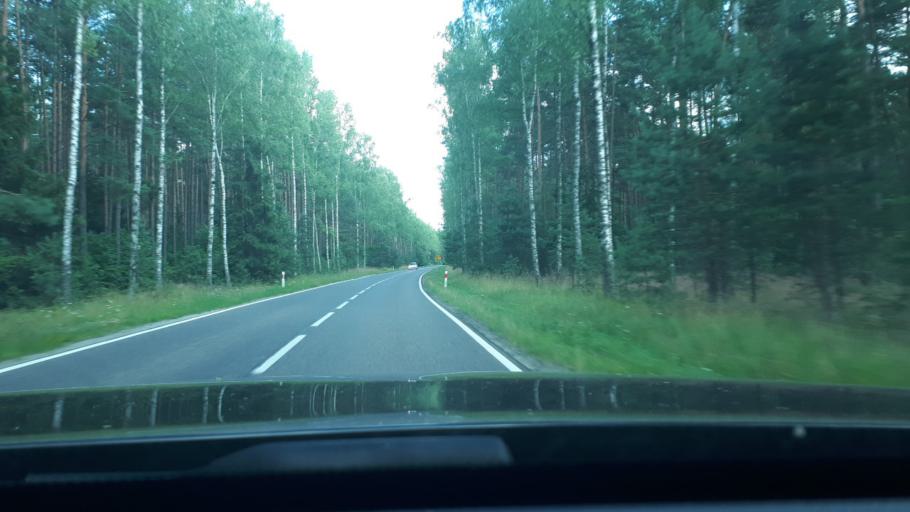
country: PL
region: Warmian-Masurian Voivodeship
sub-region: Powiat olsztynski
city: Stawiguda
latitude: 53.5326
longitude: 20.4362
